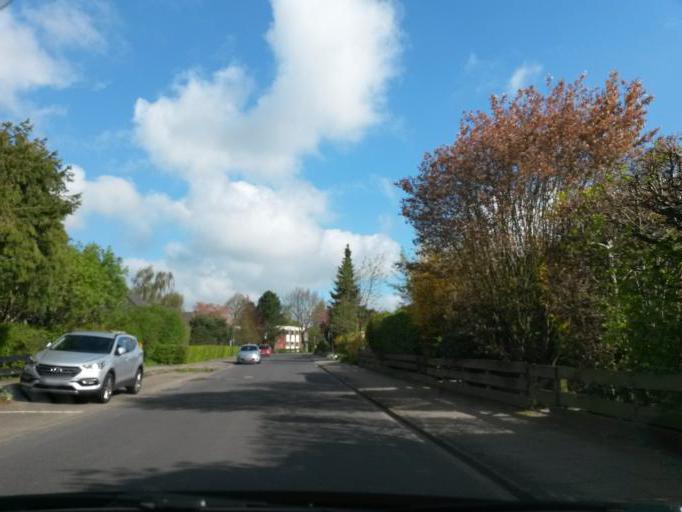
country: DE
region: Schleswig-Holstein
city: Wedel
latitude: 53.5901
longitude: 9.6866
